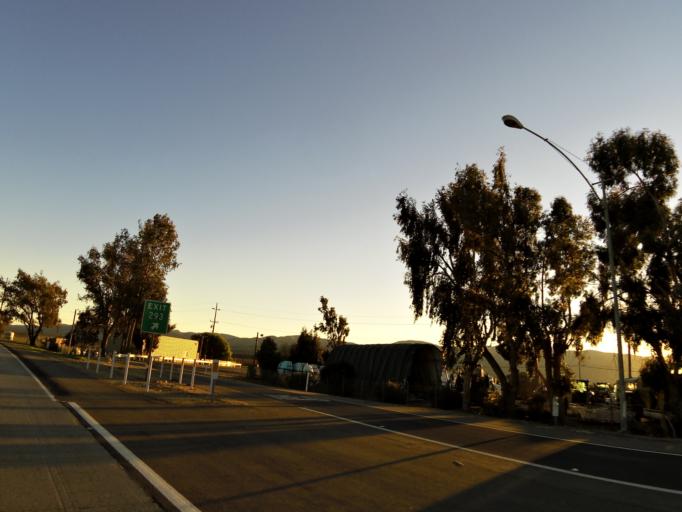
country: US
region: California
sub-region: Monterey County
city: Greenfield
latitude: 36.3140
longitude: -121.2343
